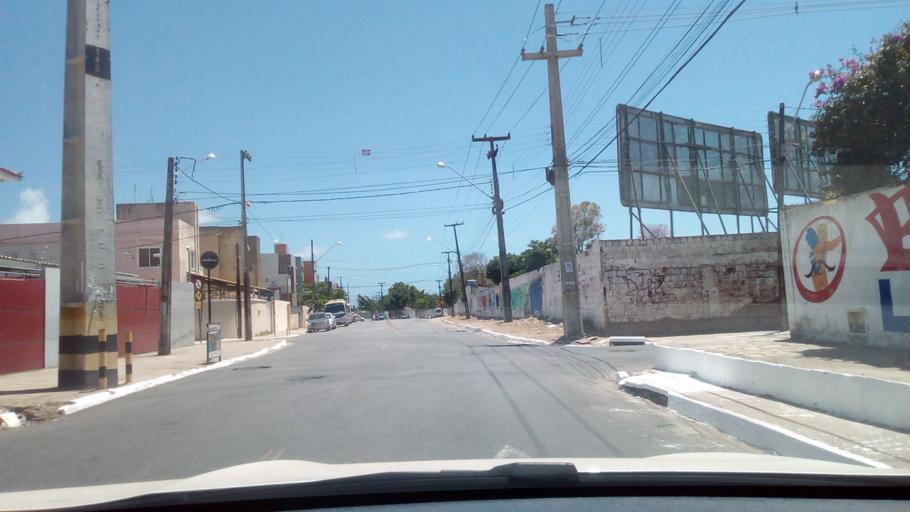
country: BR
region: Paraiba
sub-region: Joao Pessoa
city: Joao Pessoa
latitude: -7.1596
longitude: -34.8364
